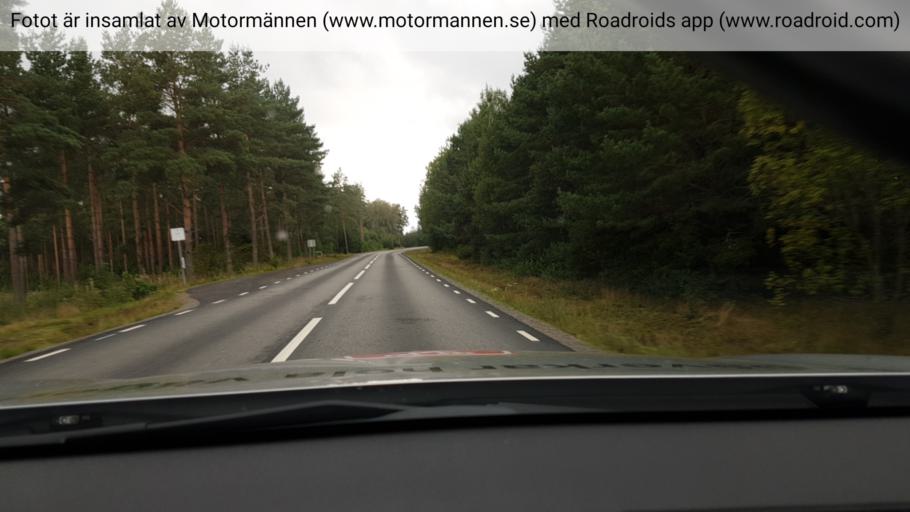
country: SE
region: Vaestra Goetaland
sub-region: Essunga Kommun
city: Nossebro
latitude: 58.1659
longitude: 12.6619
